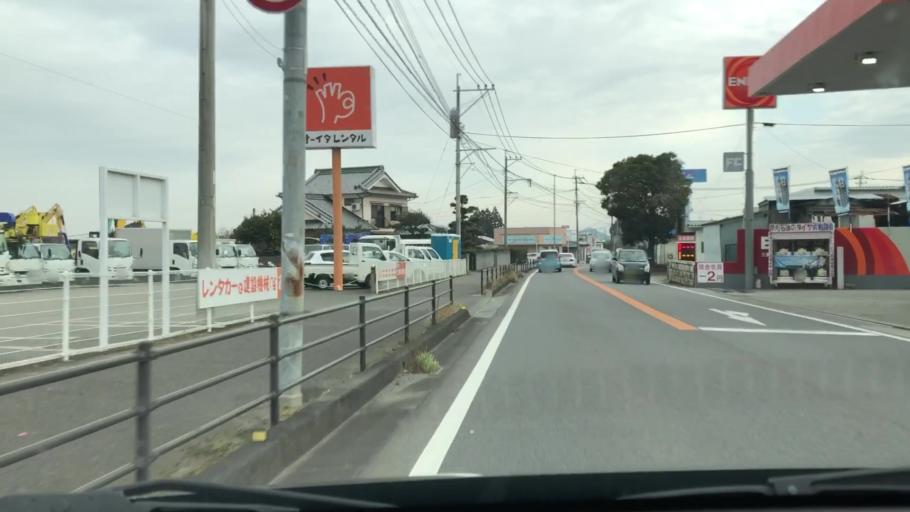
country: JP
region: Oita
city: Takedamachi
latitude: 32.9906
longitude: 131.6097
